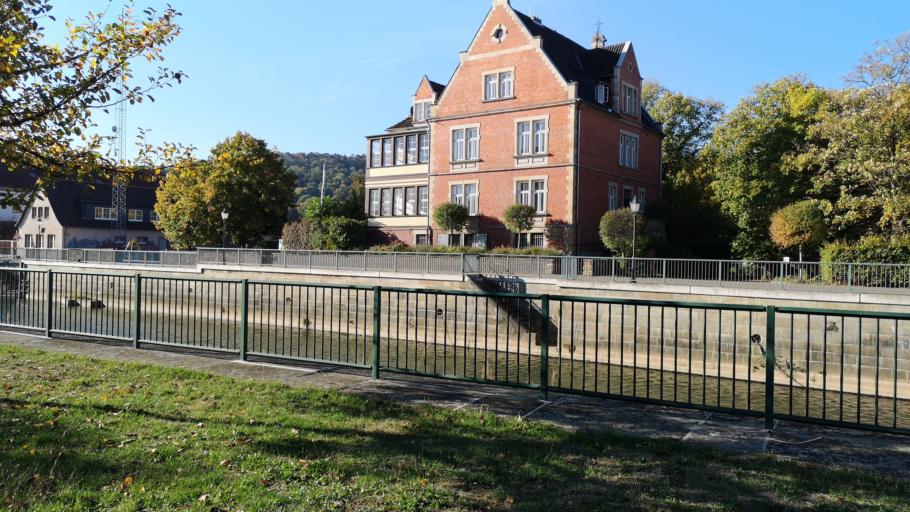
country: DE
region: Lower Saxony
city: Hameln
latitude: 52.1034
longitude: 9.3521
